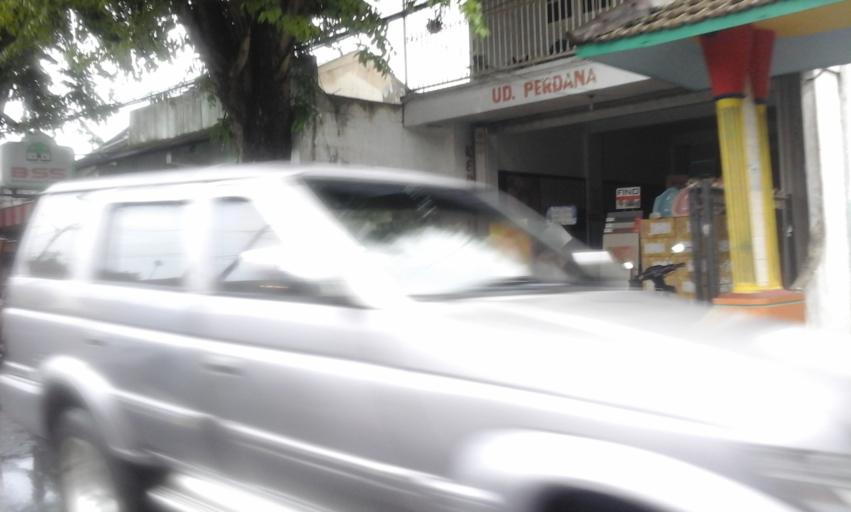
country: ID
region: East Java
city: Lumajang
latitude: -8.1282
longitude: 113.2289
